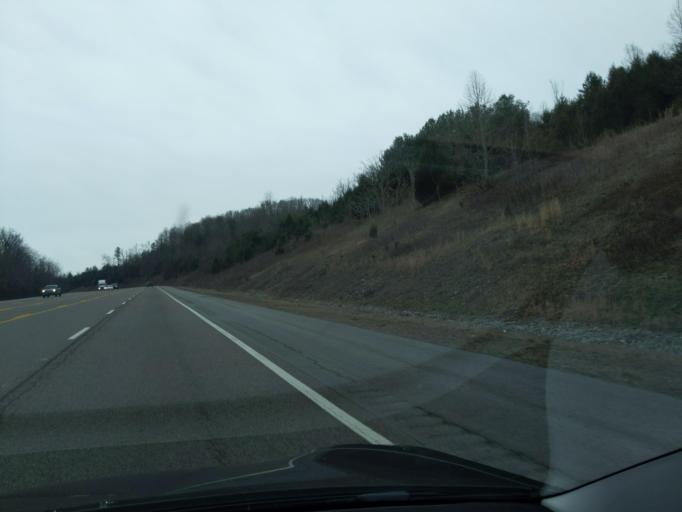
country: US
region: Tennessee
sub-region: Claiborne County
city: Tazewell
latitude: 36.5092
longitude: -83.6044
